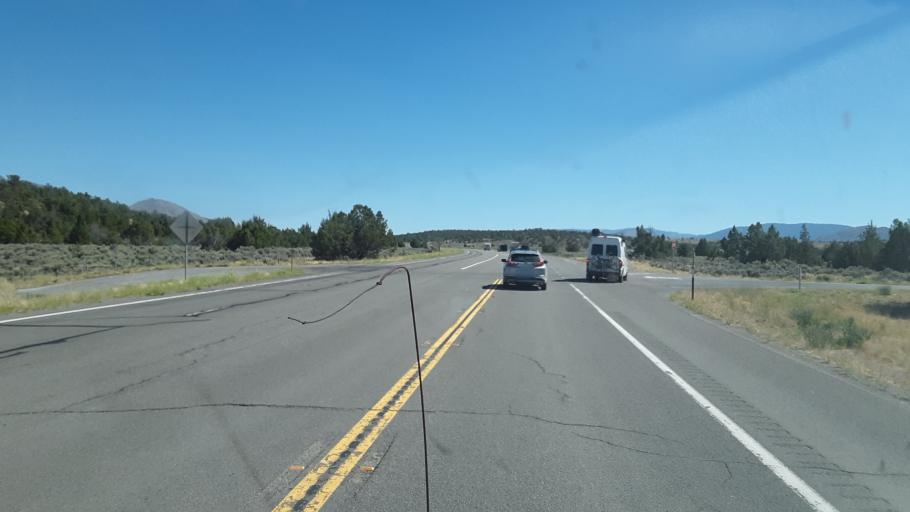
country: US
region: Nevada
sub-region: Washoe County
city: Cold Springs
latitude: 39.8525
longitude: -120.0437
